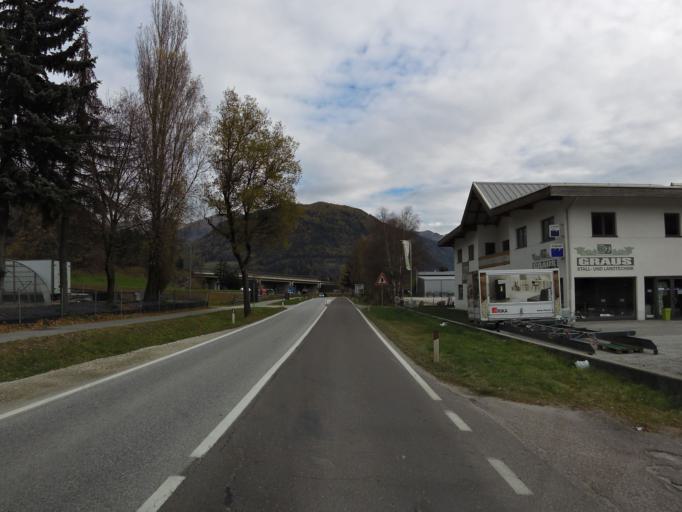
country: IT
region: Trentino-Alto Adige
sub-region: Bolzano
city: Vipiteno
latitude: 46.8869
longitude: 11.4242
